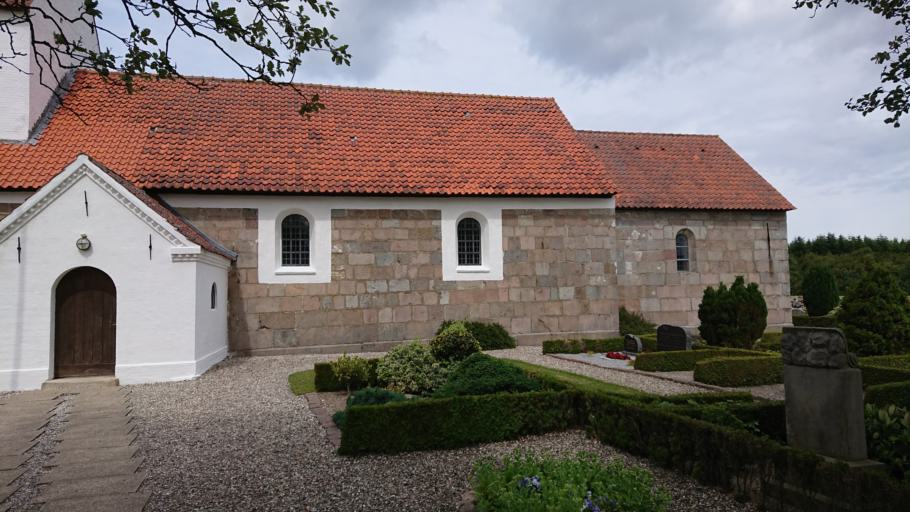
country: DK
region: North Denmark
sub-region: Jammerbugt Kommune
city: Brovst
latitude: 57.1258
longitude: 9.4202
